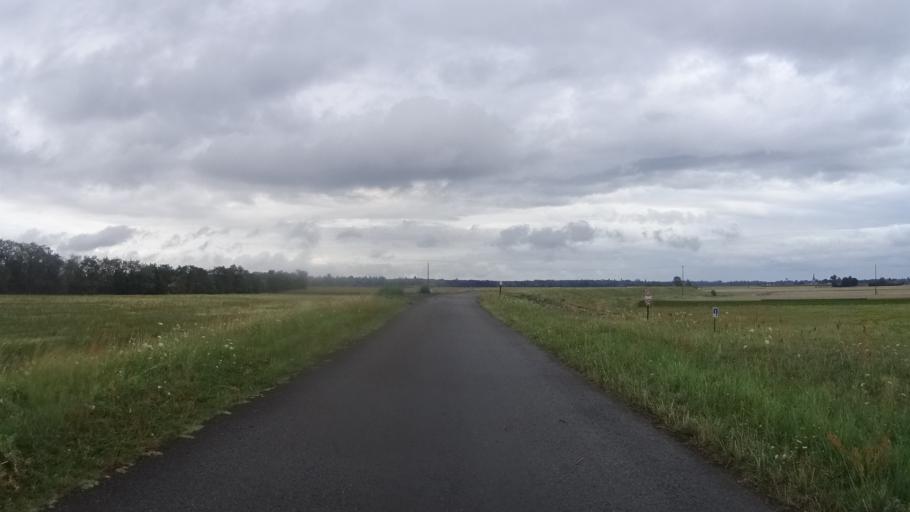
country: FR
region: Centre
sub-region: Departement du Loiret
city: Mardie
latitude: 47.8585
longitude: 2.0694
